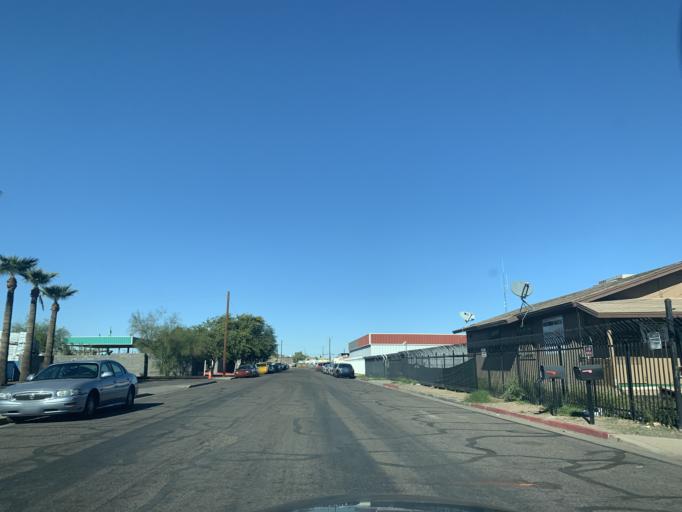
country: US
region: Arizona
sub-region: Maricopa County
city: Tempe Junction
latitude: 33.4192
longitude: -111.9852
